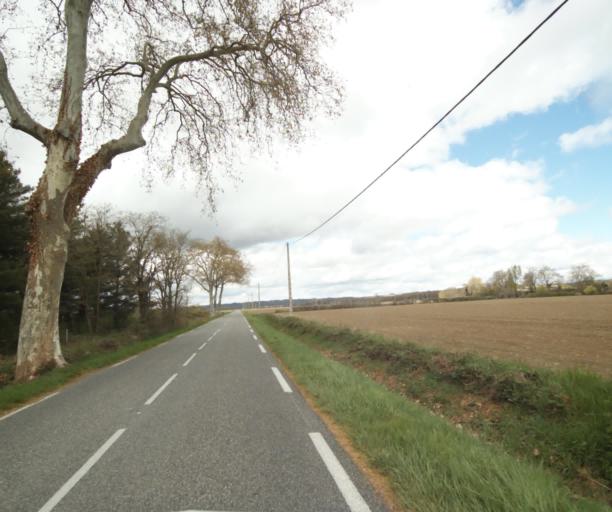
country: FR
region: Midi-Pyrenees
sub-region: Departement de l'Ariege
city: Mazeres
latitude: 43.2429
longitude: 1.6373
